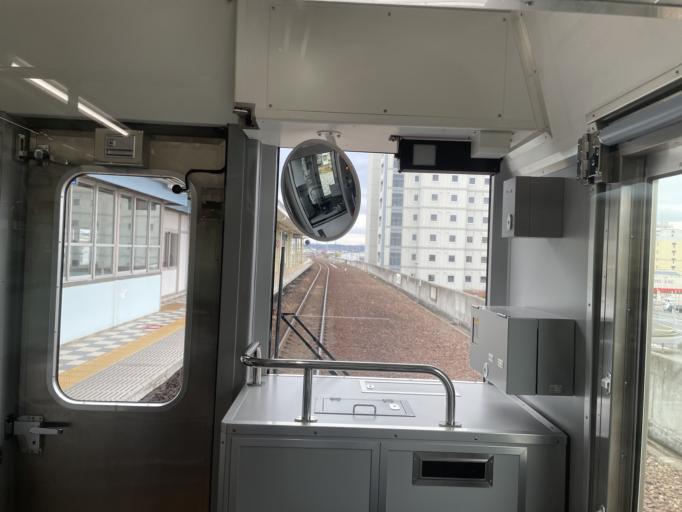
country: JP
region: Aomori
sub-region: Hachinohe Shi
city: Uchimaru
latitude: 40.5164
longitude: 141.4891
